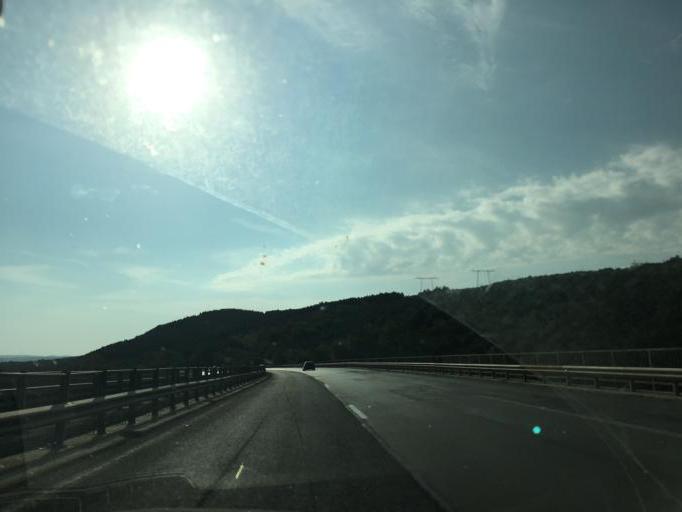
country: BG
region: Sofiya
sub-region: Obshtina Elin Pelin
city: Elin Pelin
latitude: 42.5953
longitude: 23.5903
